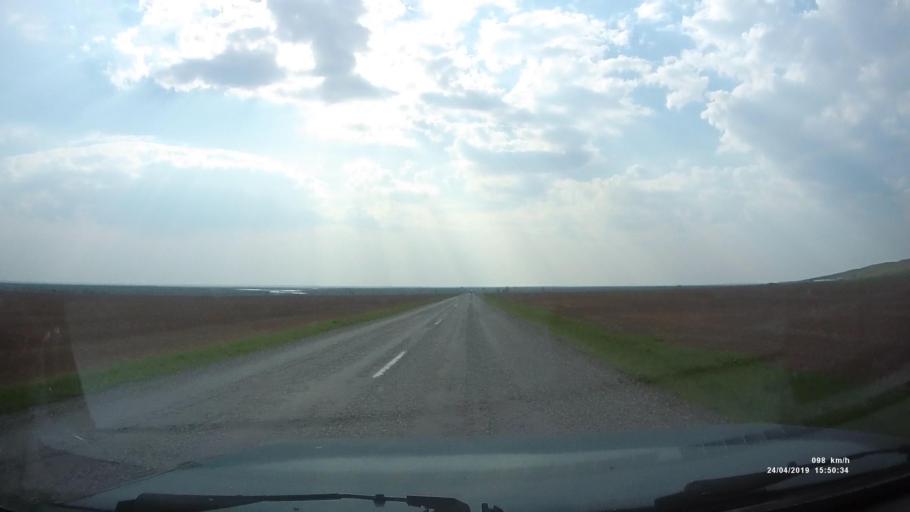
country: RU
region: Kalmykiya
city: Yashalta
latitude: 46.6042
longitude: 42.6299
